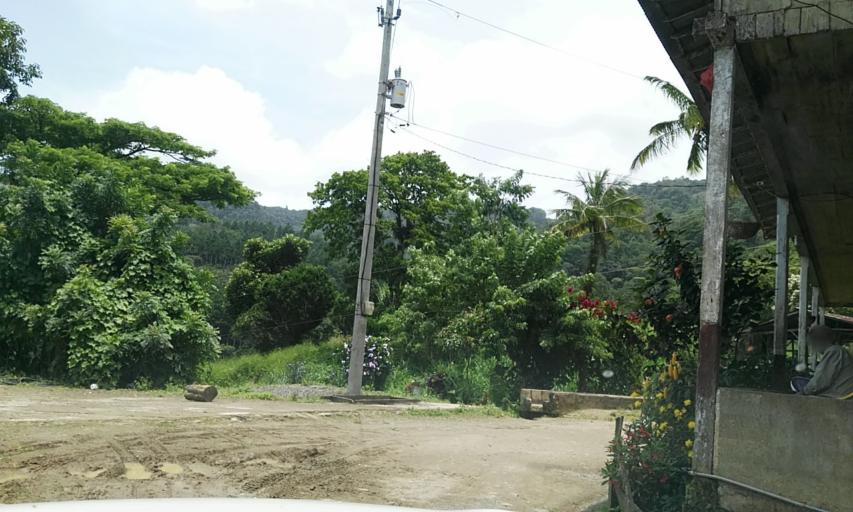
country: NI
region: Matagalpa
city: Matagalpa
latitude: 13.0188
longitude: -85.8788
